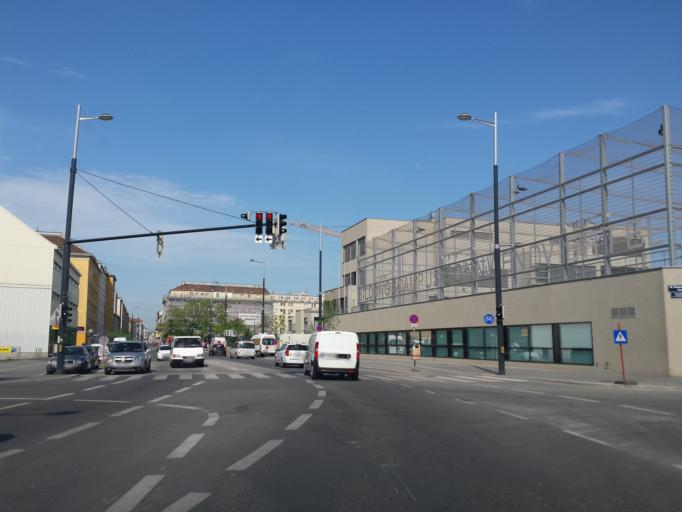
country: AT
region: Vienna
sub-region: Wien Stadt
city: Vienna
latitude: 48.1776
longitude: 16.3834
